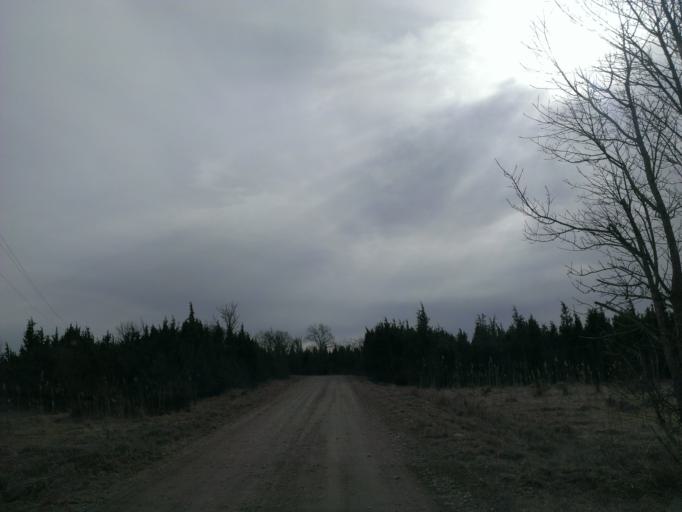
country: EE
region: Laeaene
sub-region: Lihula vald
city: Lihula
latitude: 58.5670
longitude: 23.5469
